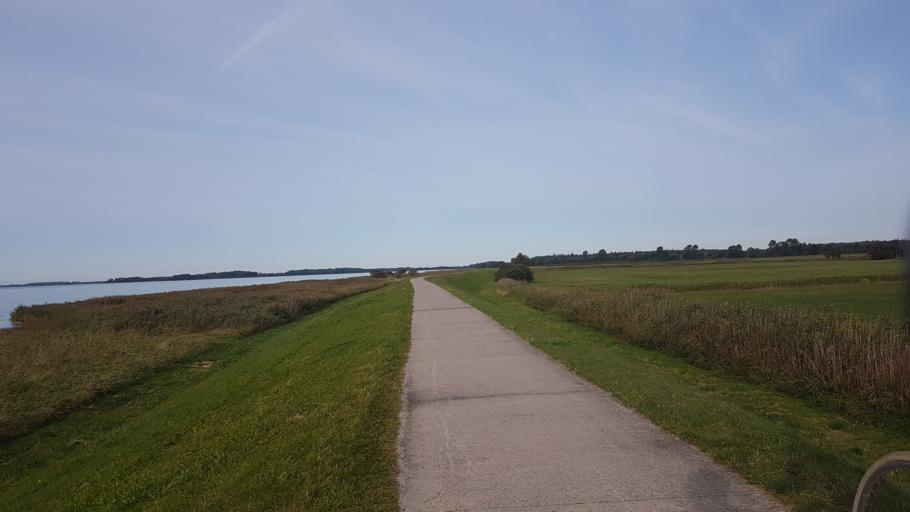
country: DE
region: Mecklenburg-Vorpommern
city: Hiddensee
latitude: 54.4790
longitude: 13.1471
